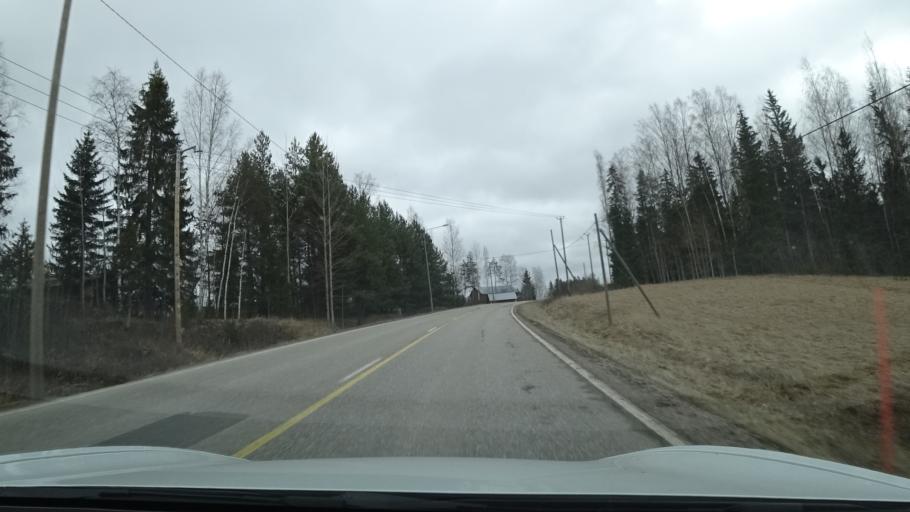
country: FI
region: Uusimaa
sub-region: Porvoo
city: Pukkila
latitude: 60.6555
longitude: 25.6767
